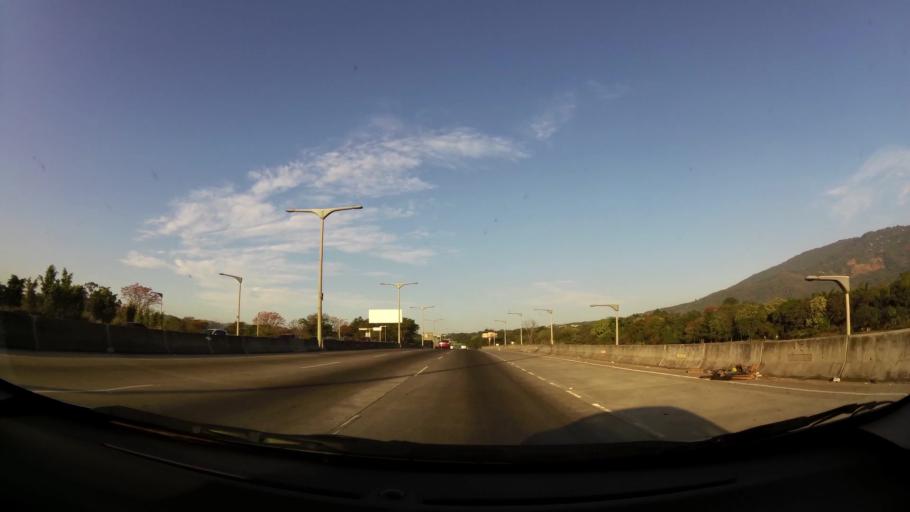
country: SV
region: La Libertad
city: Antiguo Cuscatlan
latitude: 13.6851
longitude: -89.2519
